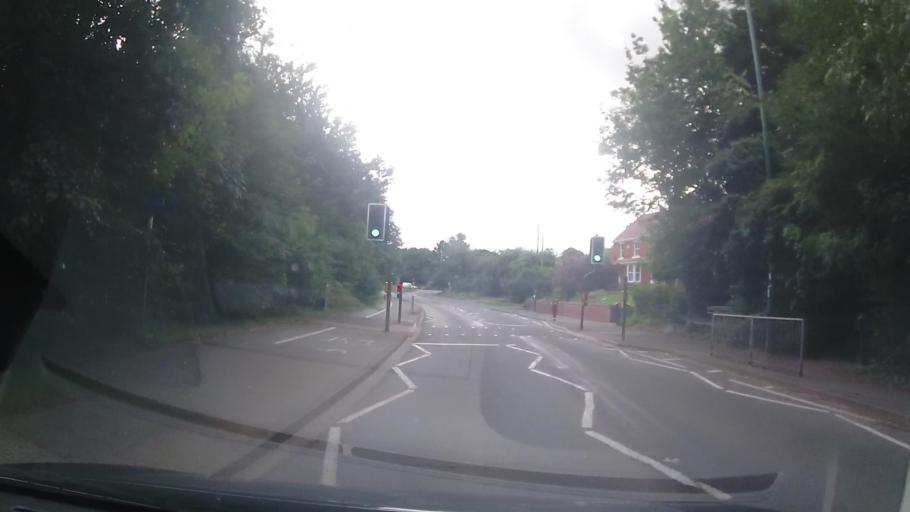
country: GB
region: England
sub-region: Shropshire
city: Bayston Hill
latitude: 52.6997
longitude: -2.7838
